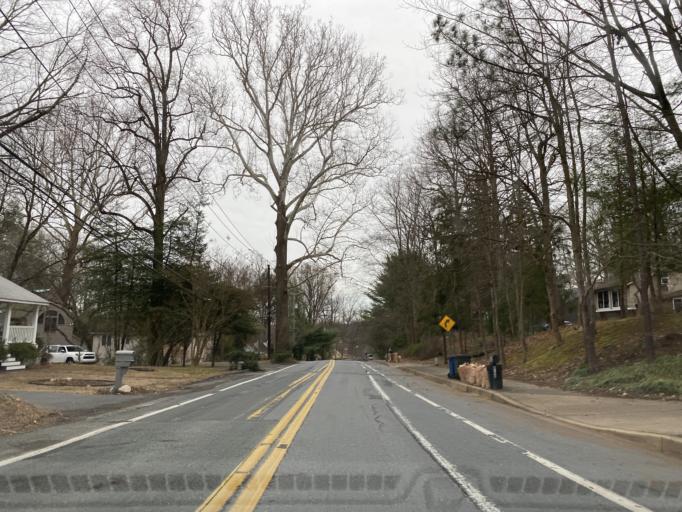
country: US
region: Maryland
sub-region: Montgomery County
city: Cabin John
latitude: 38.9763
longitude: -77.1693
